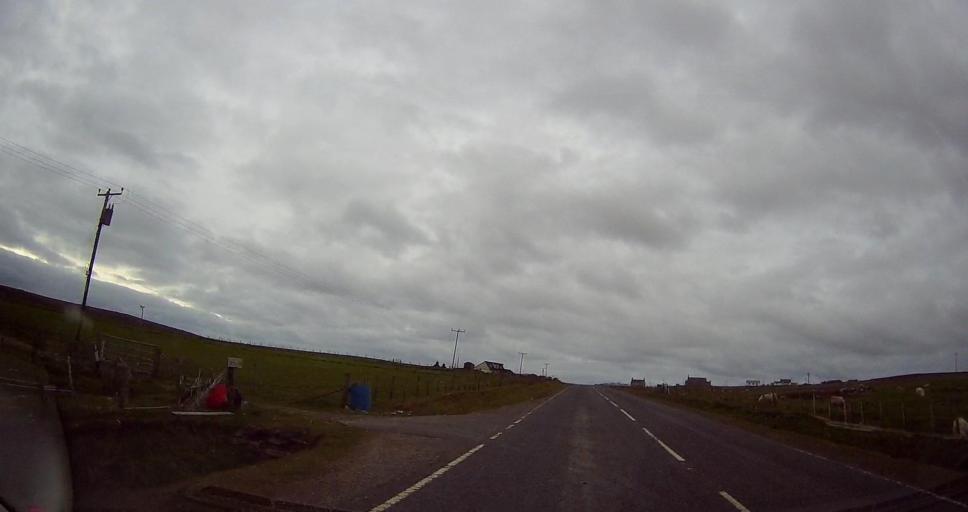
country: GB
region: Scotland
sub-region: Shetland Islands
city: Shetland
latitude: 60.6620
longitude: -1.0515
